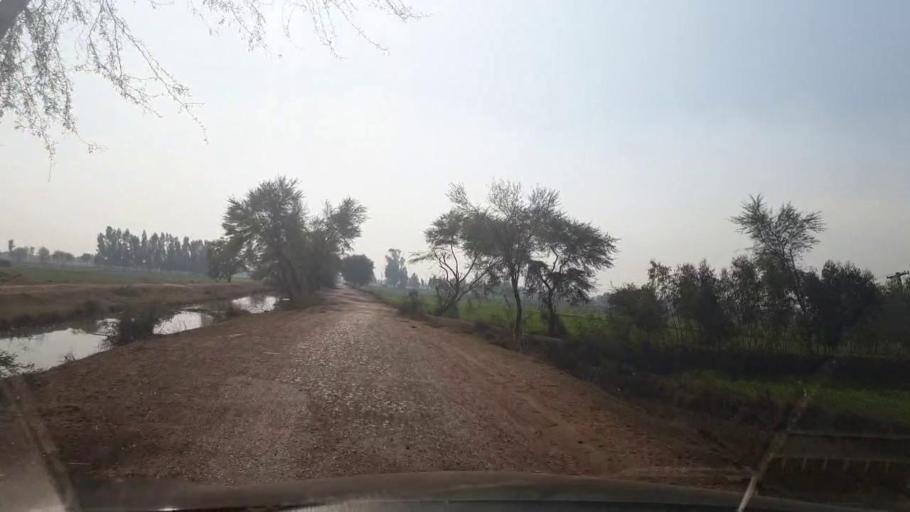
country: PK
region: Sindh
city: Khairpur
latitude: 28.1308
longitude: 69.6464
